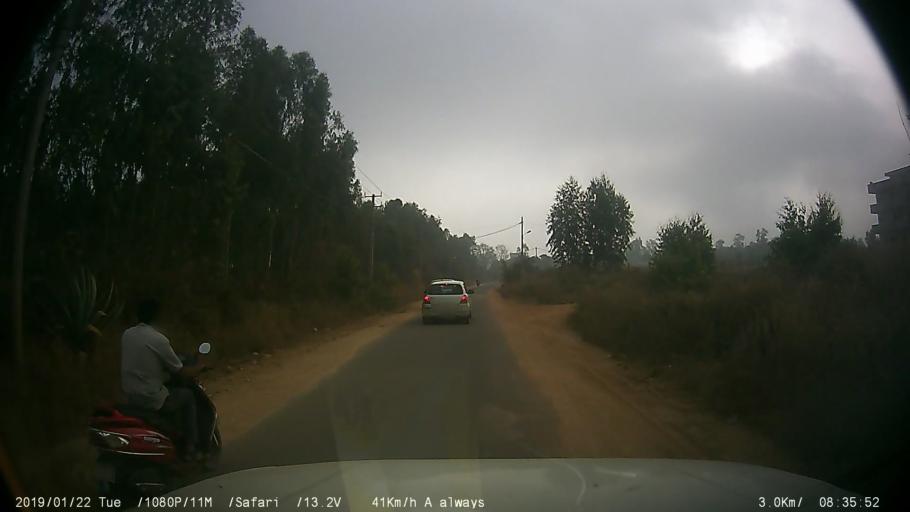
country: IN
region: Karnataka
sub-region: Bangalore Urban
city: Anekal
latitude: 12.8196
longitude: 77.6445
